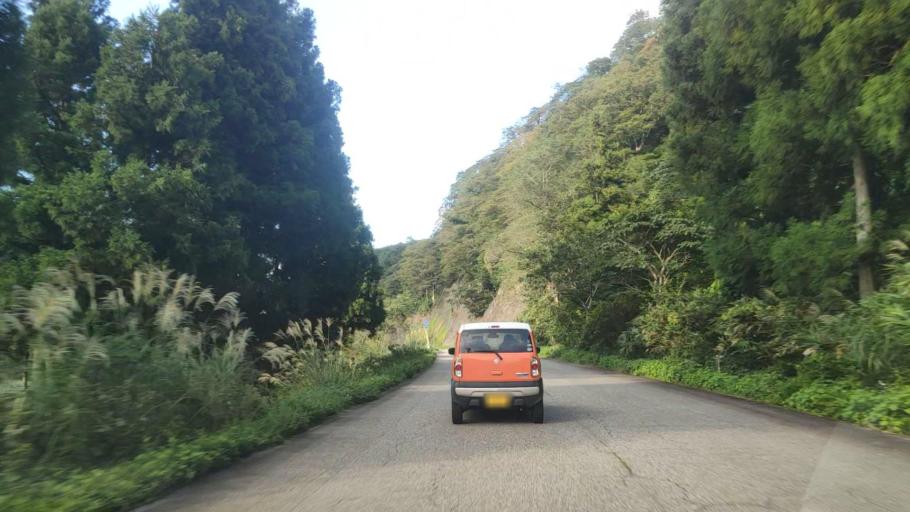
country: JP
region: Toyama
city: Yatsuomachi-higashikumisaka
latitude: 36.4504
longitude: 137.0847
